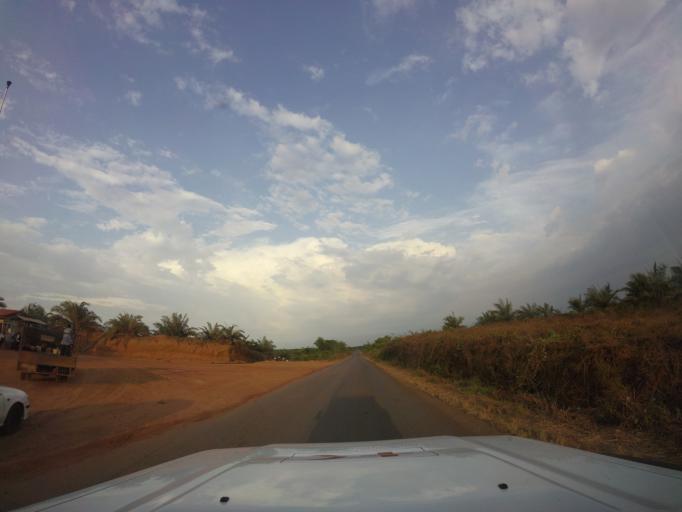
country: LR
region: Bomi
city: Tubmanburg
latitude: 6.7123
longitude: -10.9612
